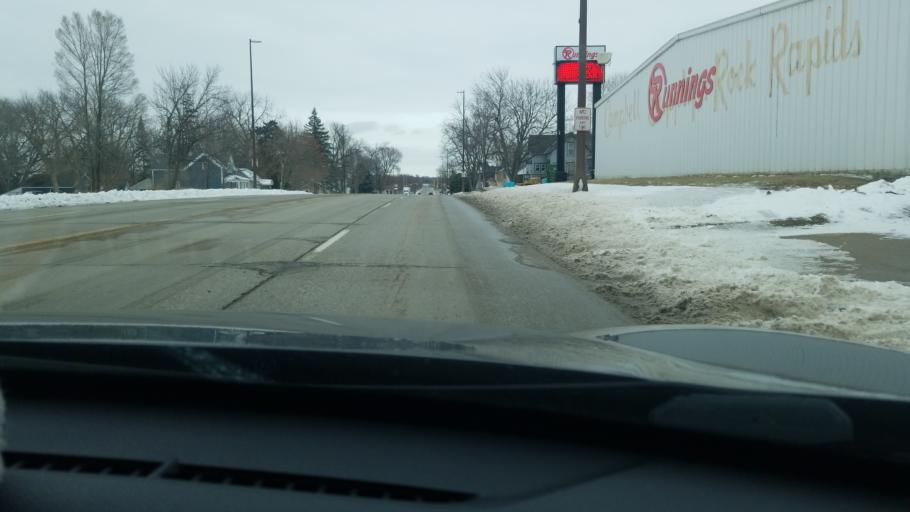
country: US
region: Iowa
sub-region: Lyon County
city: Rock Rapids
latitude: 43.4319
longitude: -96.1806
